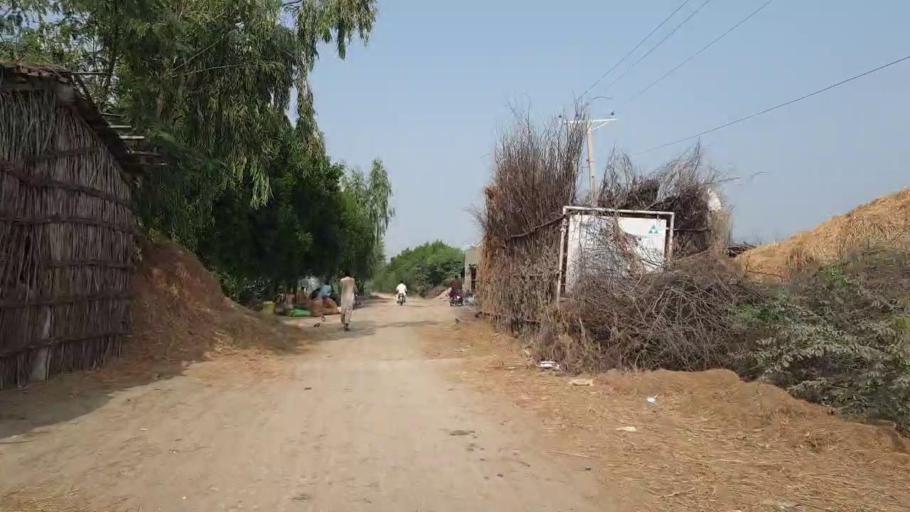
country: PK
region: Sindh
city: Kario
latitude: 24.9245
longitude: 68.6010
